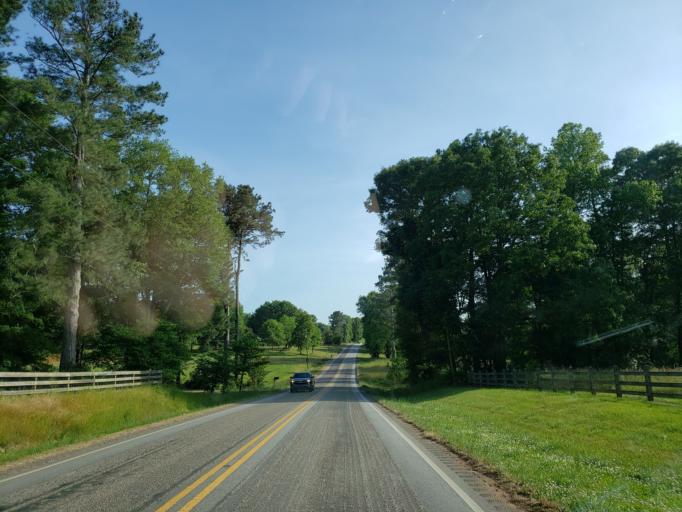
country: US
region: Georgia
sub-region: Carroll County
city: Bowdon
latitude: 33.4630
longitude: -85.3115
